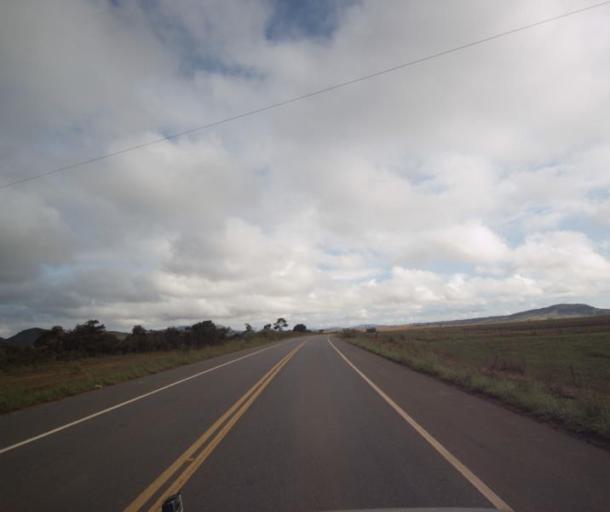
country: BR
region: Goias
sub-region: Barro Alto
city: Barro Alto
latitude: -15.2929
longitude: -48.6769
